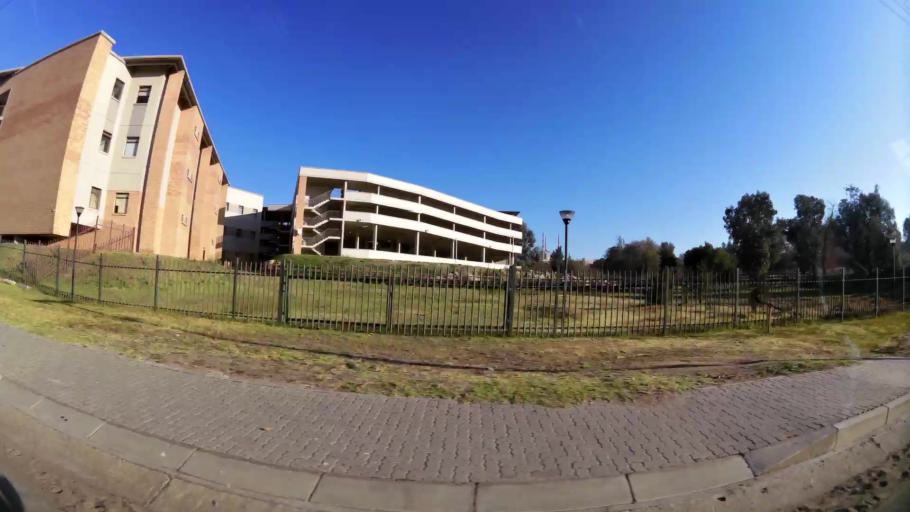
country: ZA
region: Gauteng
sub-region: City of Johannesburg Metropolitan Municipality
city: Midrand
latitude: -26.0196
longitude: 28.1344
